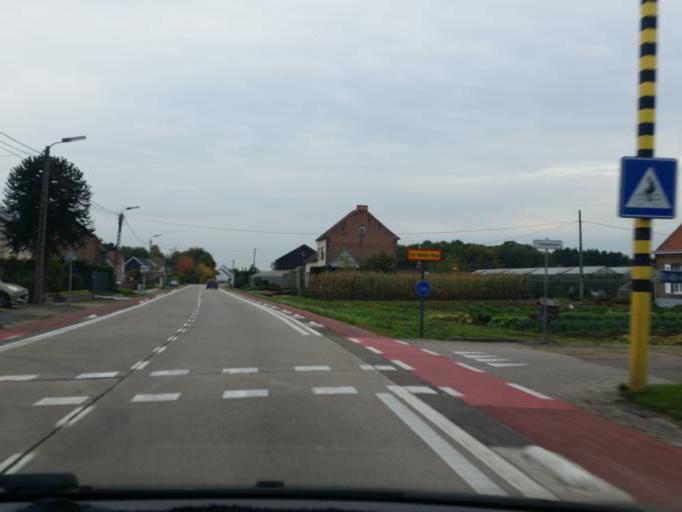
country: BE
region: Flanders
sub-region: Provincie Antwerpen
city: Sint-Katelijne-Waver
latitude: 51.0703
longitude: 4.5699
